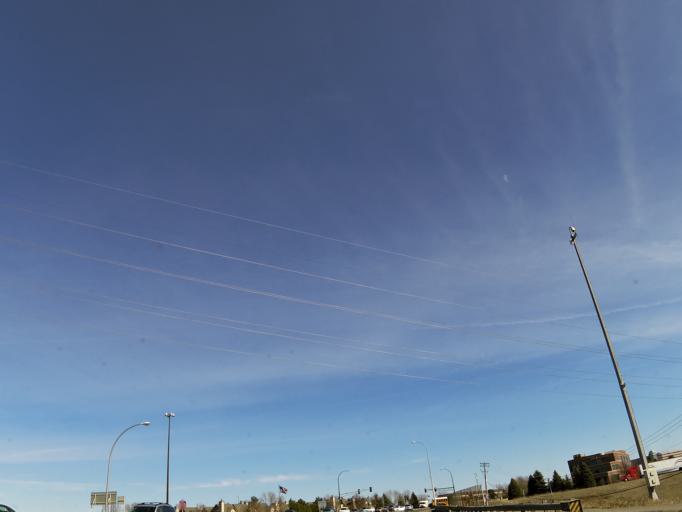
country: US
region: Minnesota
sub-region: Hennepin County
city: Eden Prairie
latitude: 44.8618
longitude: -93.4254
